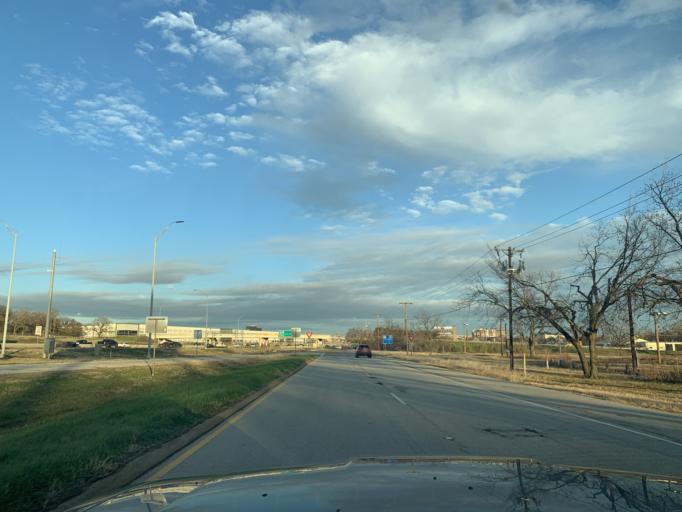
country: US
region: Texas
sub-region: Tarrant County
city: Euless
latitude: 32.8362
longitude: -97.0334
